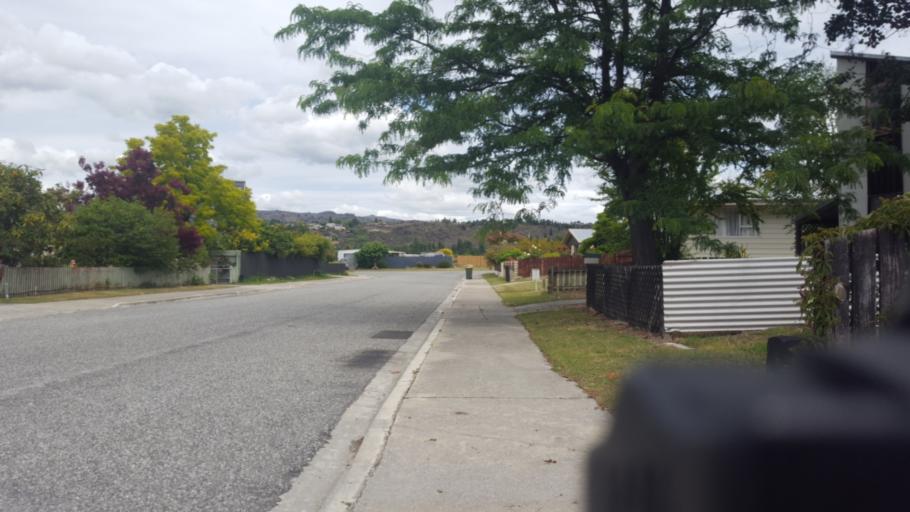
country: NZ
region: Otago
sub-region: Queenstown-Lakes District
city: Wanaka
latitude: -45.2486
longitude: 169.3775
